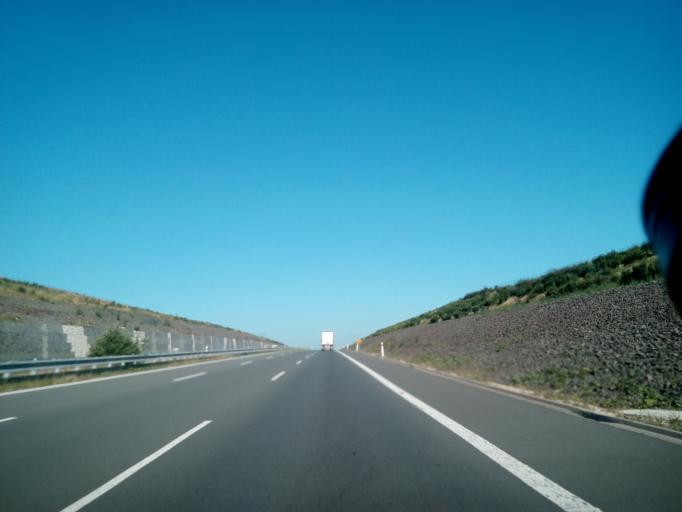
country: SK
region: Presovsky
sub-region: Okres Presov
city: Presov
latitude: 49.0050
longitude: 21.1529
